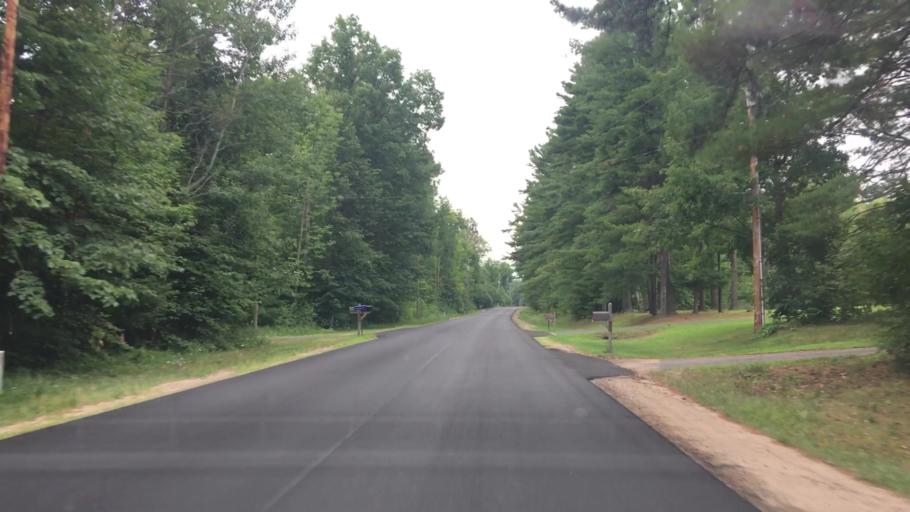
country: US
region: New York
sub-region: Clinton County
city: Peru
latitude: 44.5575
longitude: -73.5665
